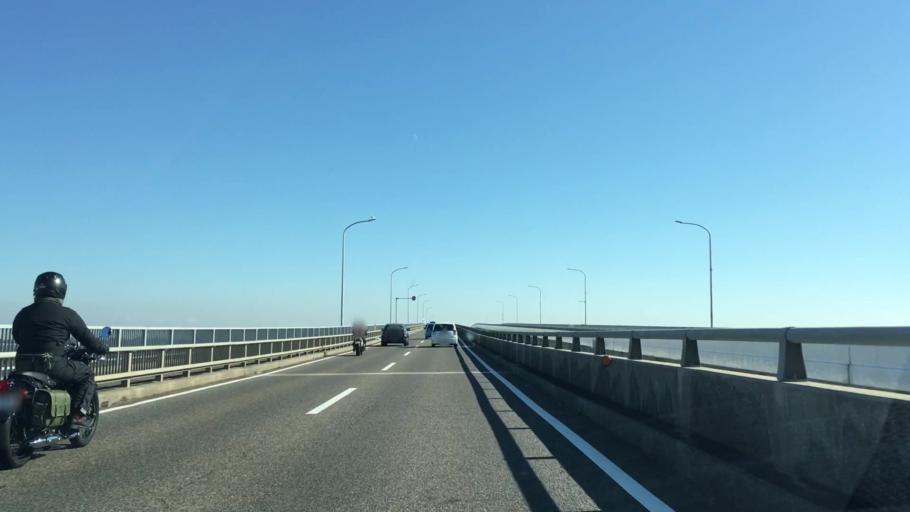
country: JP
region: Aichi
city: Tahara
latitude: 34.6932
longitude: 137.3005
